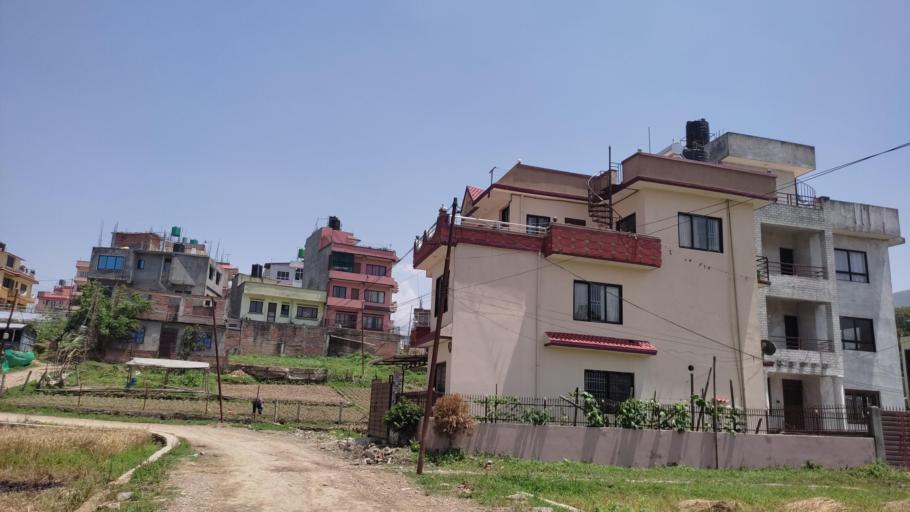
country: NP
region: Central Region
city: Kirtipur
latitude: 27.6687
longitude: 85.2661
